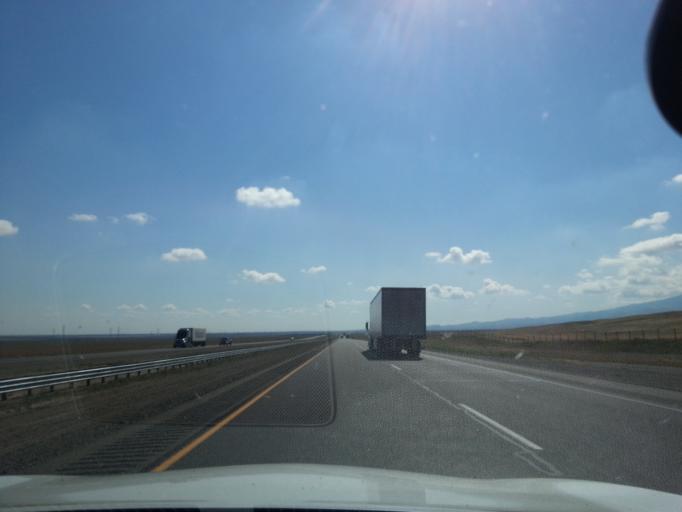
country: US
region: California
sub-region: Fresno County
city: San Joaquin
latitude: 36.4709
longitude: -120.4271
